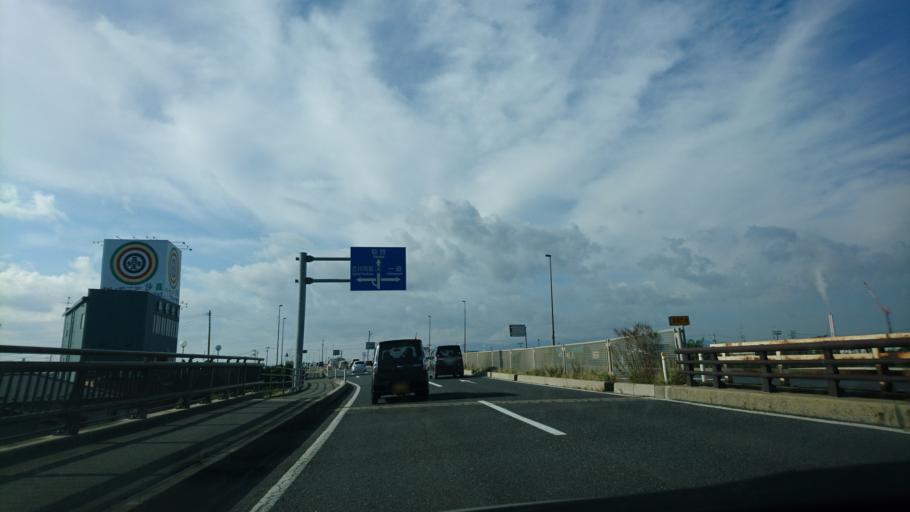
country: JP
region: Miyagi
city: Furukawa
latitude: 38.5984
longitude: 140.9689
